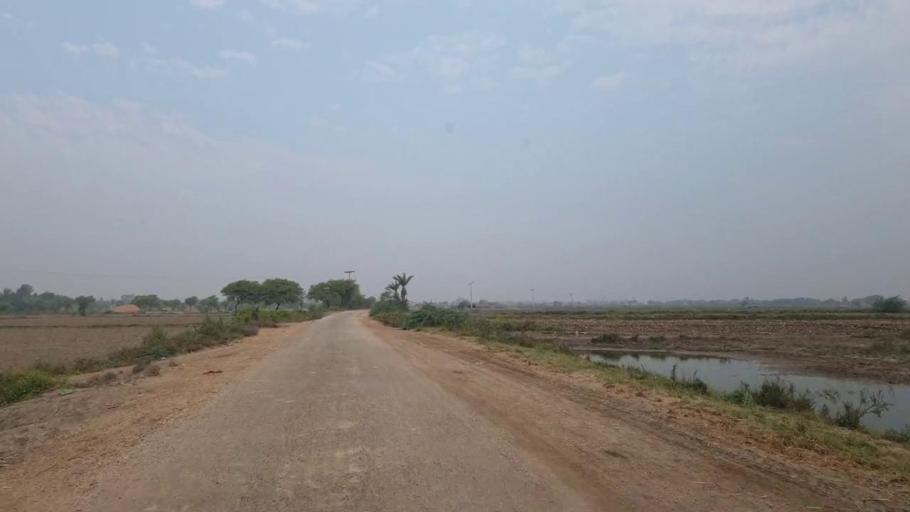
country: PK
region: Sindh
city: Tando Bago
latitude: 24.7832
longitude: 68.8879
